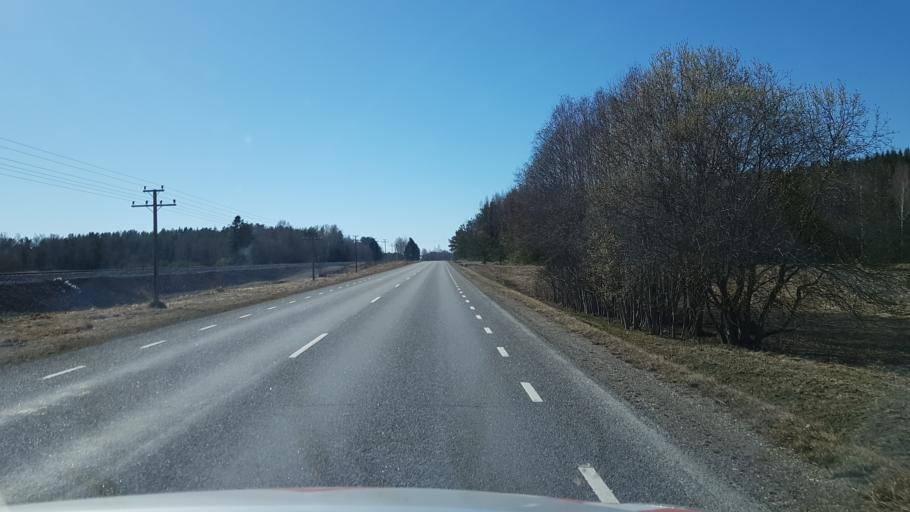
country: EE
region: Ida-Virumaa
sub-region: Aseri vald
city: Aseri
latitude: 59.3479
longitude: 26.7795
